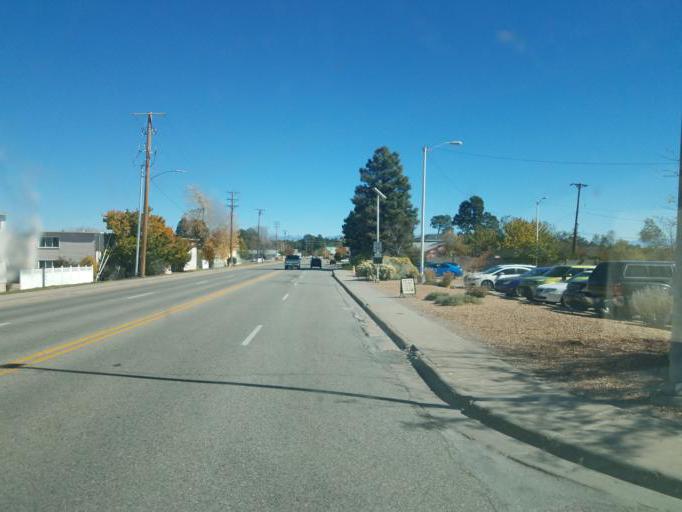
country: US
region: New Mexico
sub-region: Los Alamos County
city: Los Alamos
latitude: 35.8826
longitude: -106.3173
